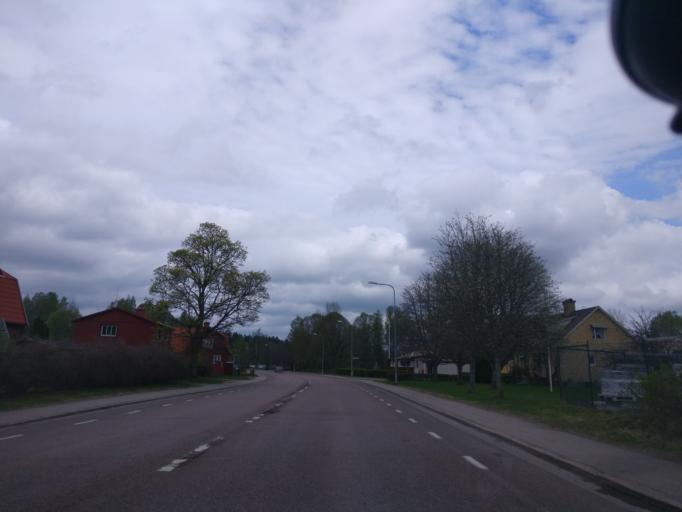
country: SE
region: Vaermland
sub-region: Hagfors Kommun
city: Ekshaerad
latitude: 60.1786
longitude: 13.4962
